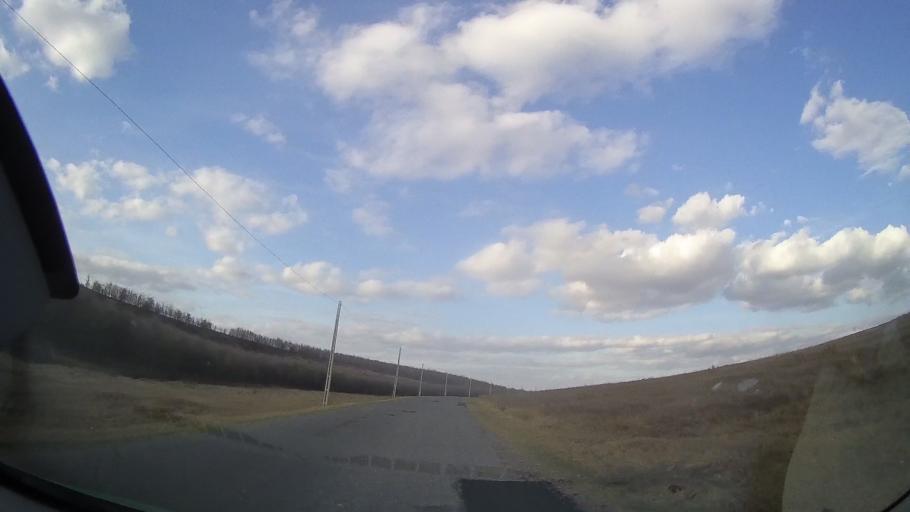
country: RO
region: Constanta
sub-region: Comuna Cerchezu
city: Cerchezu
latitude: 43.8303
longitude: 28.0963
